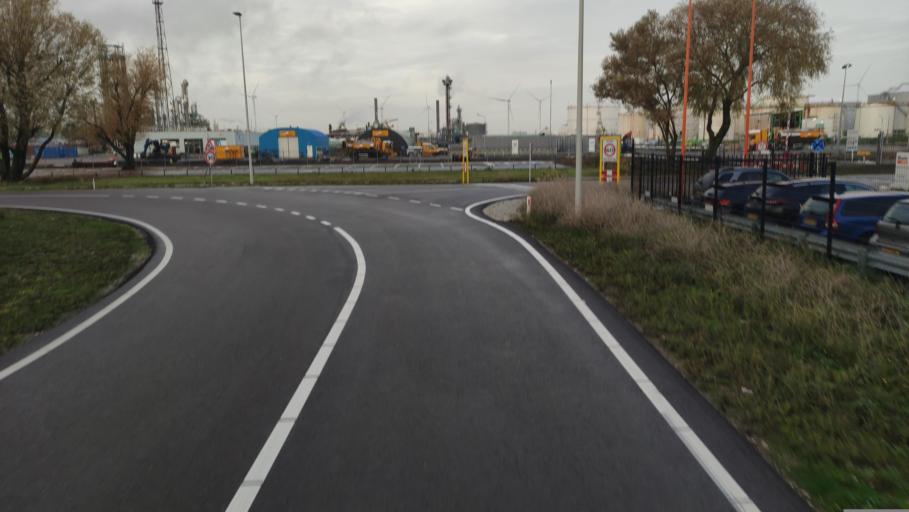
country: NL
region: South Holland
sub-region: Gemeente Brielle
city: Brielle
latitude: 51.9250
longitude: 4.1875
